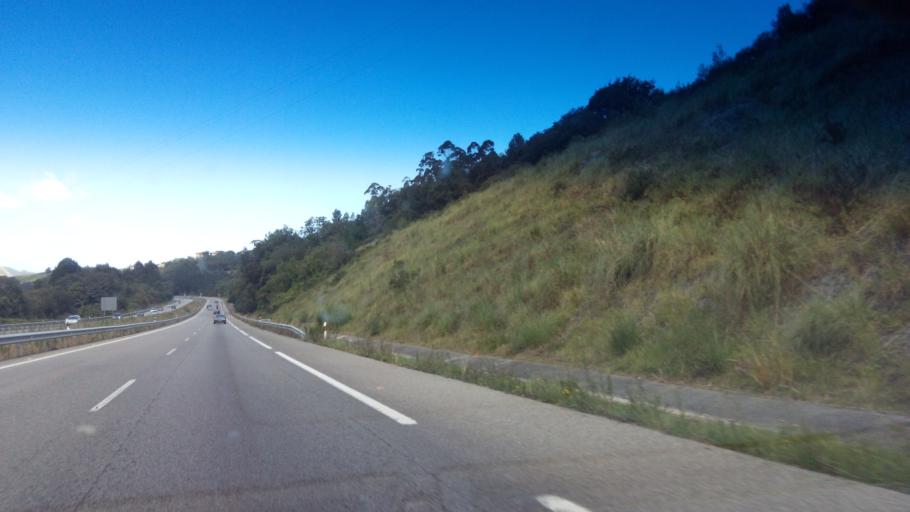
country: ES
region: Asturias
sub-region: Province of Asturias
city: Ribadesella
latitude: 43.4371
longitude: -5.0710
